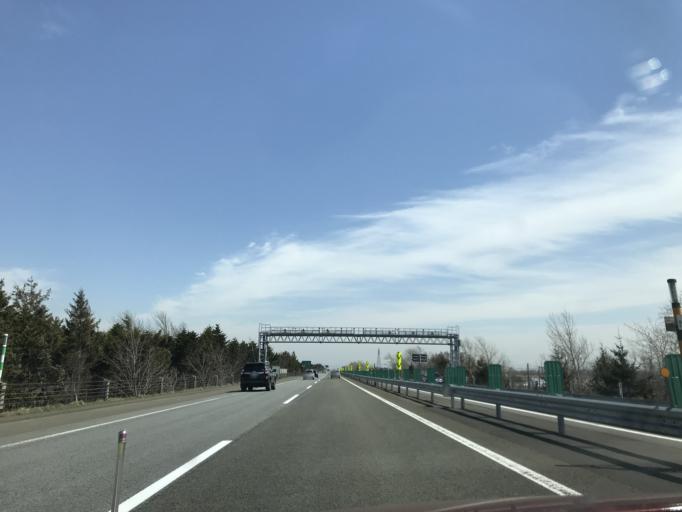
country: JP
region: Hokkaido
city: Ebetsu
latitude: 43.0974
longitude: 141.5853
